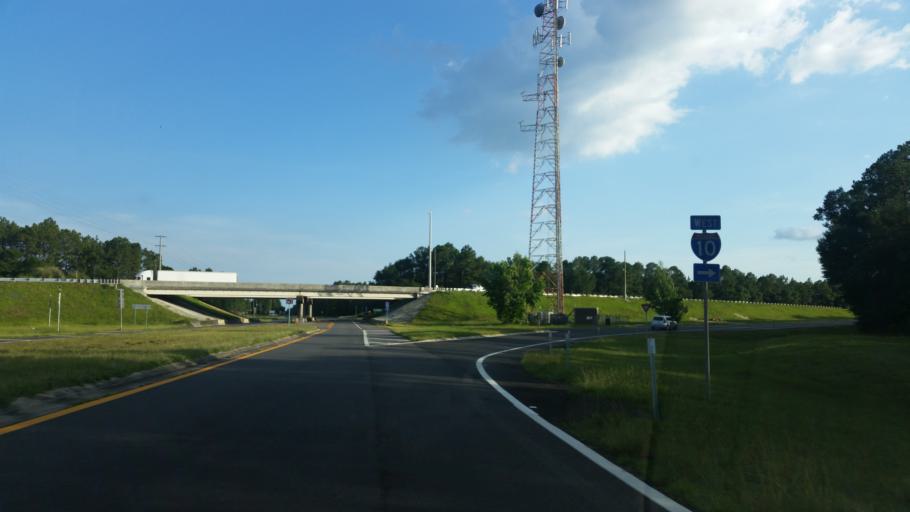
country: US
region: Florida
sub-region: Okaloosa County
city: Crestview
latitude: 30.7001
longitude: -86.7513
